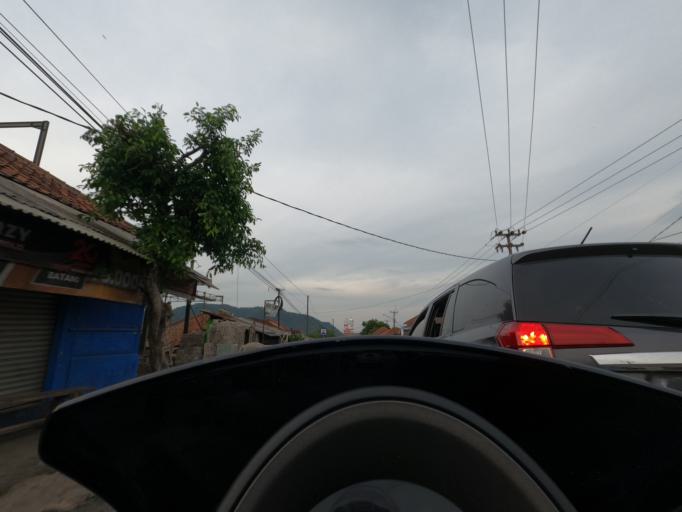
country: ID
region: West Java
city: Lembang
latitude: -6.6623
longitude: 107.7097
